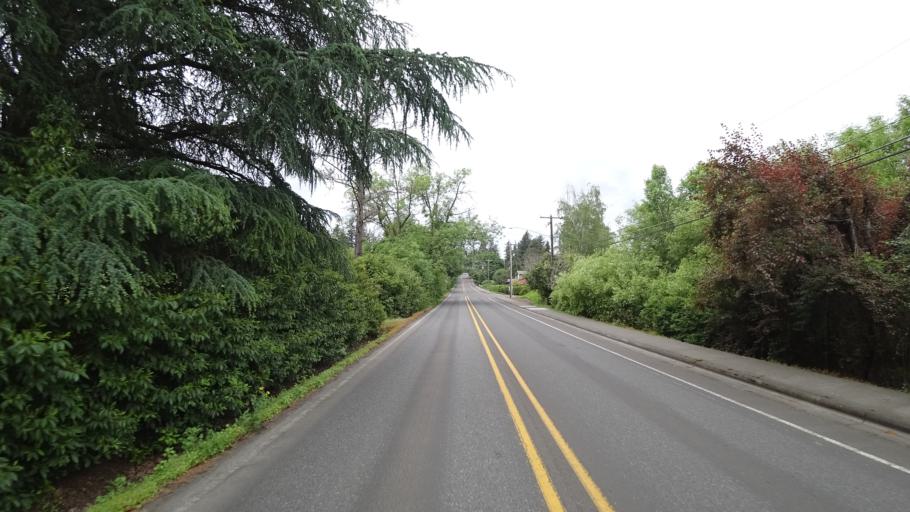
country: US
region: Oregon
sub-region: Washington County
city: Raleigh Hills
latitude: 45.4776
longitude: -122.7596
